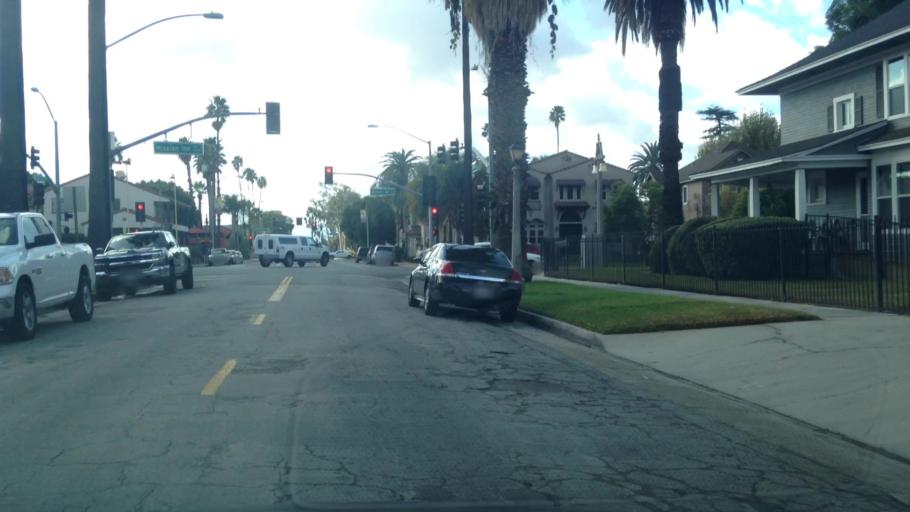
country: US
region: California
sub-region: Riverside County
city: Rubidoux
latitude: 33.9856
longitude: -117.3782
